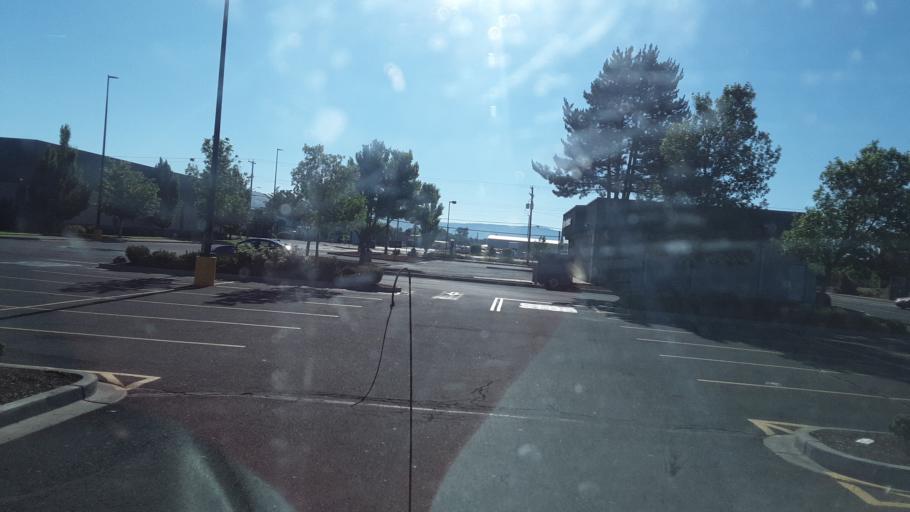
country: US
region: Oregon
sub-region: Klamath County
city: Altamont
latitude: 42.1936
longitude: -121.7587
